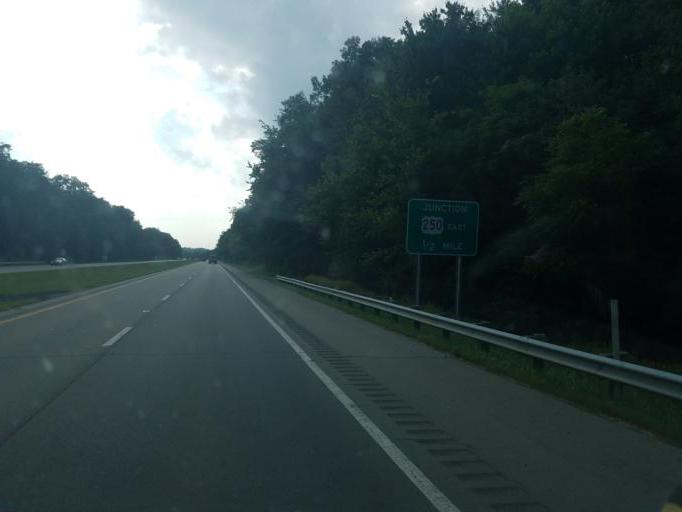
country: US
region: Ohio
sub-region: Wayne County
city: Wooster
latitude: 40.7971
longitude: -82.0013
